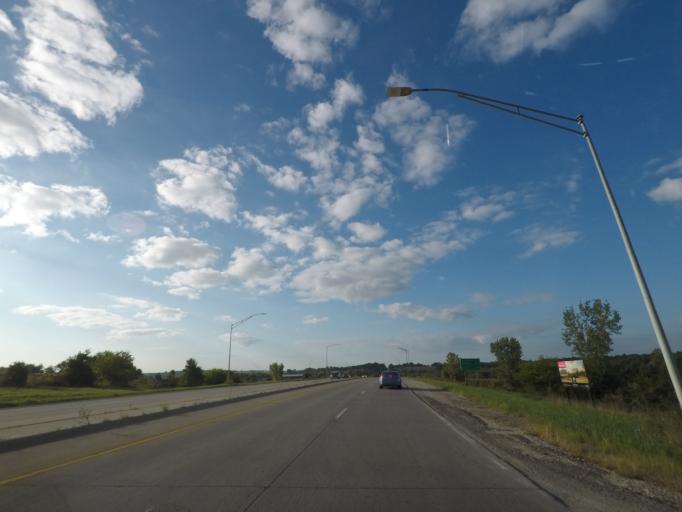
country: US
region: Iowa
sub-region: Warren County
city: Norwalk
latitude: 41.5109
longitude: -93.6451
